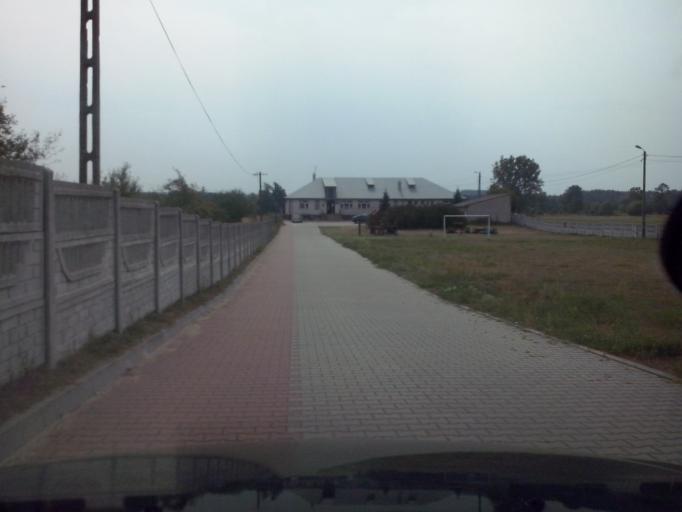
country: PL
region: Swietokrzyskie
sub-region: Powiat kielecki
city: Brzeziny
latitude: 50.7551
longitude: 20.5599
